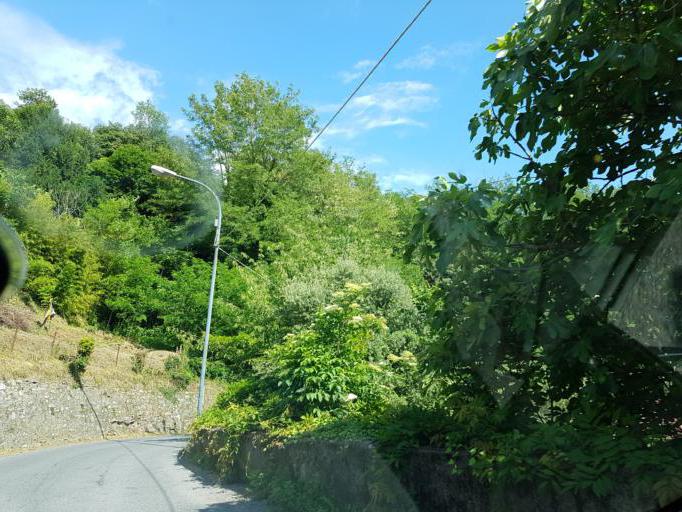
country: IT
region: Liguria
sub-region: Provincia di Genova
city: Genoa
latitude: 44.4592
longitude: 8.8889
